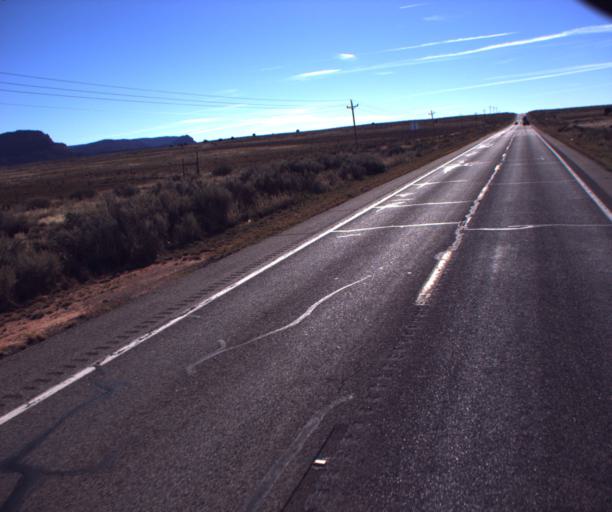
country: US
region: Arizona
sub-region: Mohave County
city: Colorado City
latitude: 36.9217
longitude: -112.9364
